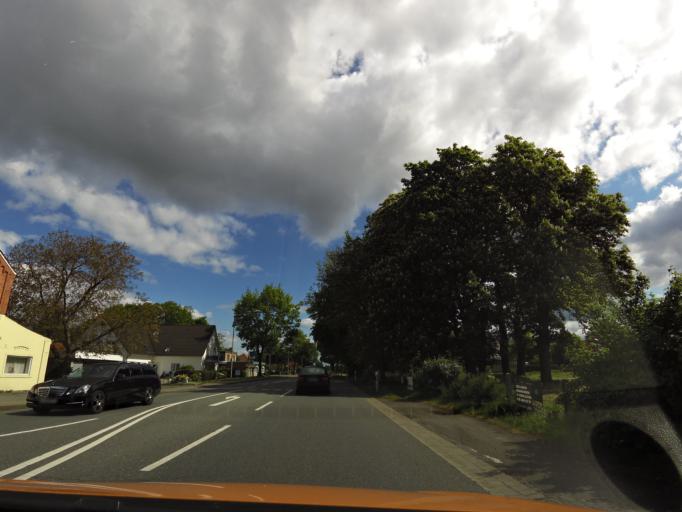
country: DE
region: Lower Saxony
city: Stuhr
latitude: 52.9895
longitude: 8.7581
